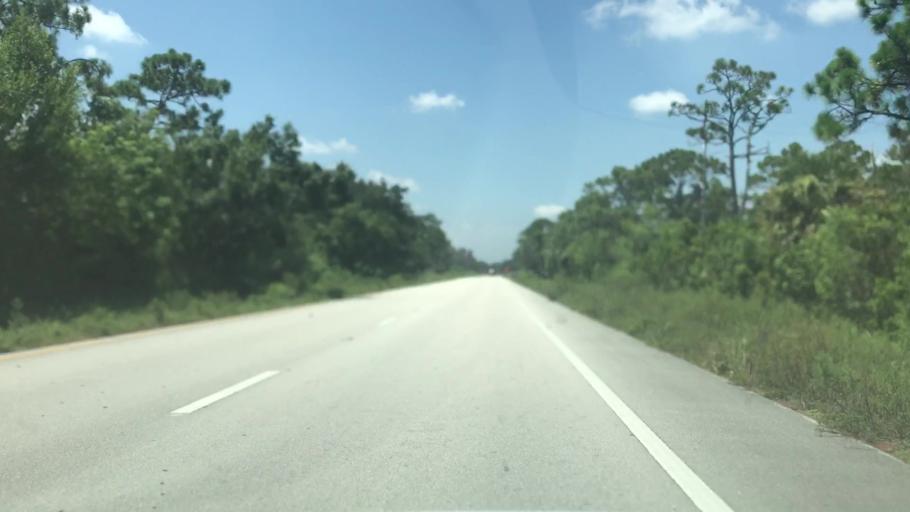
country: US
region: Florida
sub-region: Saint Lucie County
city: Lakewood Park
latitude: 27.5517
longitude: -80.3723
